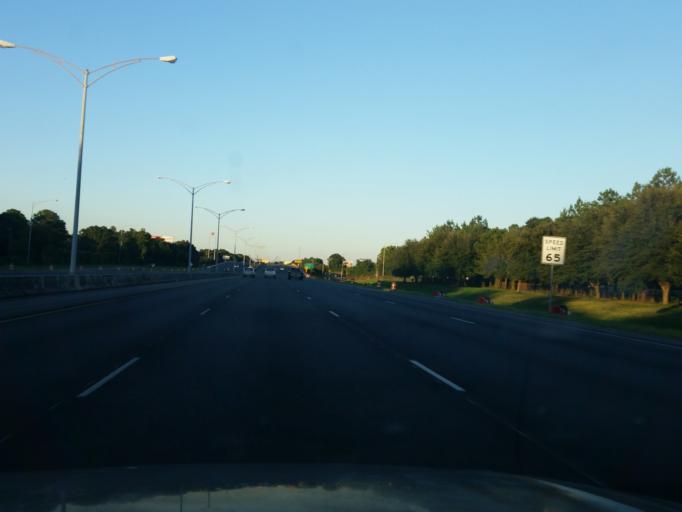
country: US
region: Alabama
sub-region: Mobile County
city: Mobile
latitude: 30.6581
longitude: -88.0625
